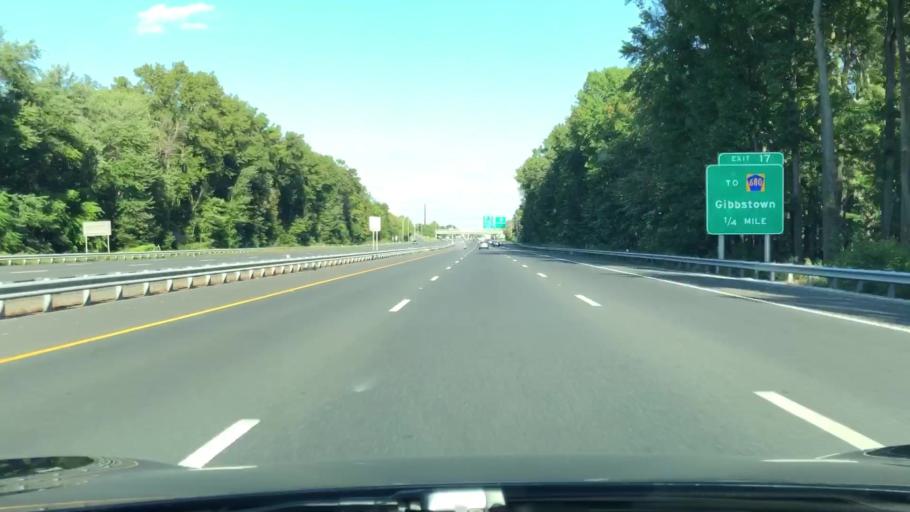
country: US
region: New Jersey
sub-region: Gloucester County
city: Gibbstown
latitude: 39.8133
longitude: -75.2656
